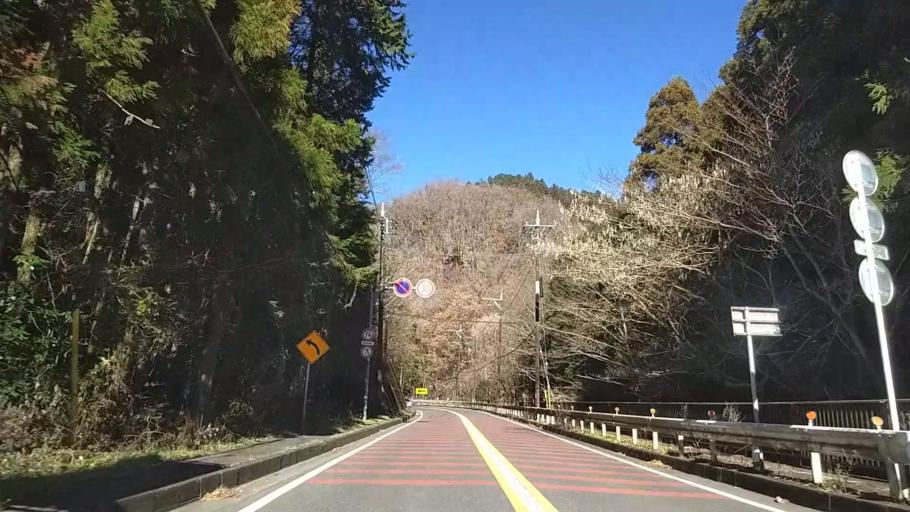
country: JP
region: Tokyo
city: Hachioji
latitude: 35.6175
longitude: 139.2400
